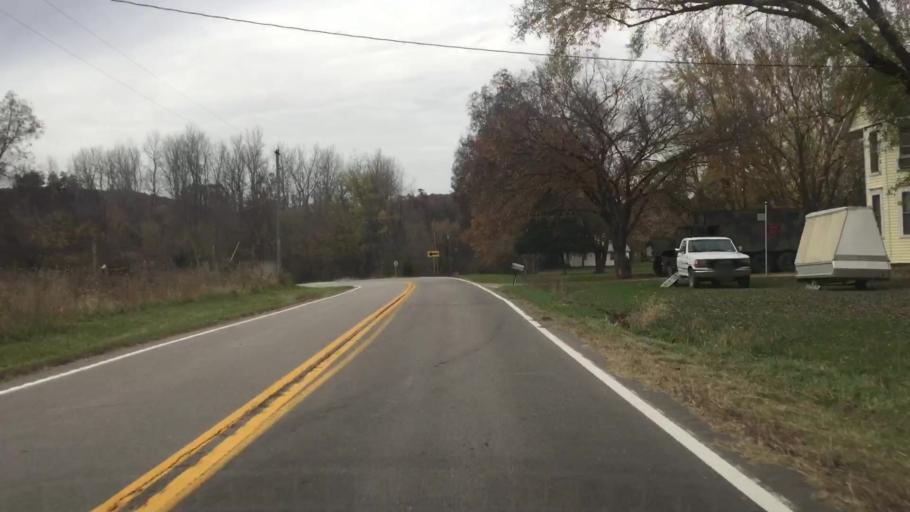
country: US
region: Missouri
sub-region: Gasconade County
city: Hermann
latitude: 38.7069
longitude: -91.6245
